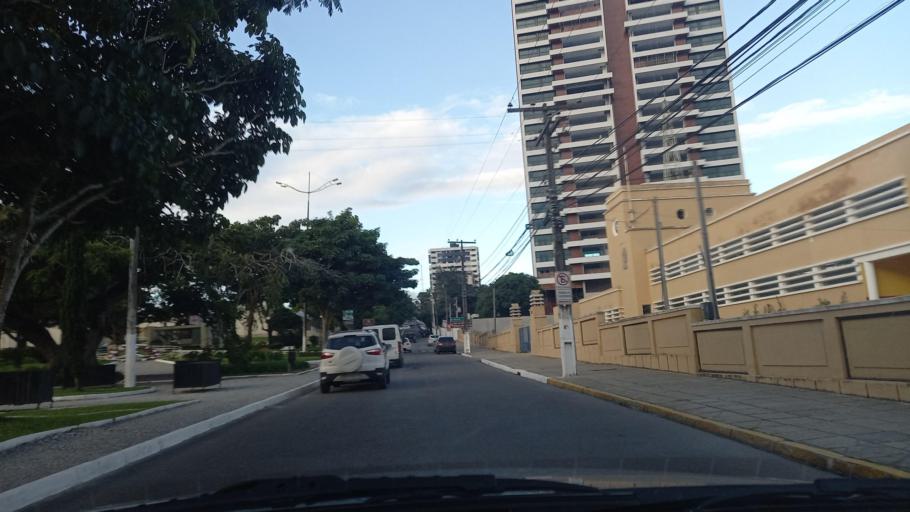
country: BR
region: Pernambuco
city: Garanhuns
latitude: -8.8822
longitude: -36.4773
